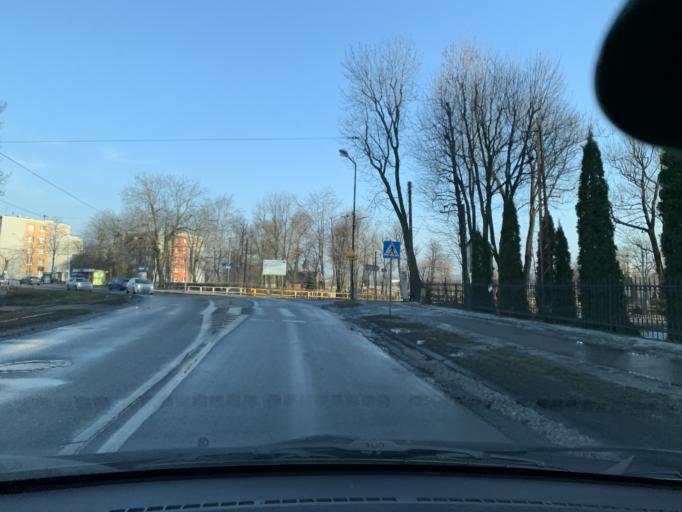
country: PL
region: Silesian Voivodeship
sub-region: Bytom
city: Bytom
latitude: 50.3364
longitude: 18.8961
